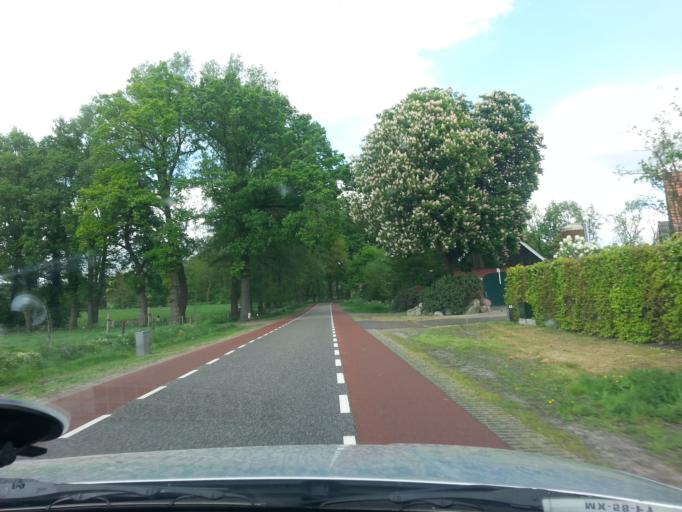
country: NL
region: Overijssel
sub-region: Gemeente Losser
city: Losser
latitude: 52.3178
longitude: 6.9967
